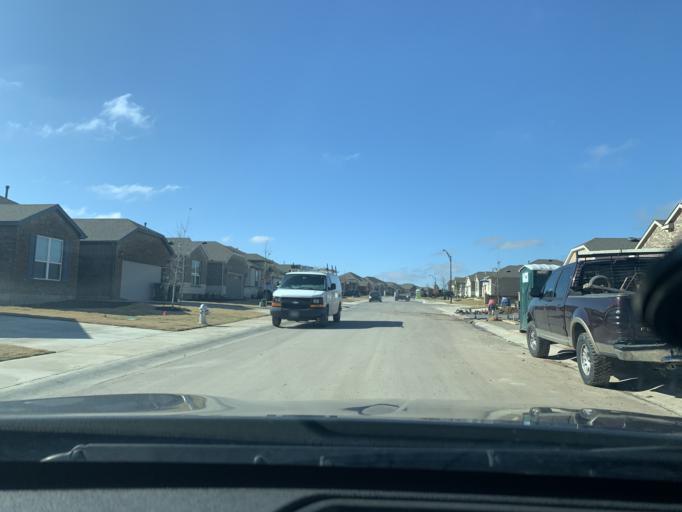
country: US
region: Texas
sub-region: Williamson County
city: Serenada
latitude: 30.7309
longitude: -97.7568
